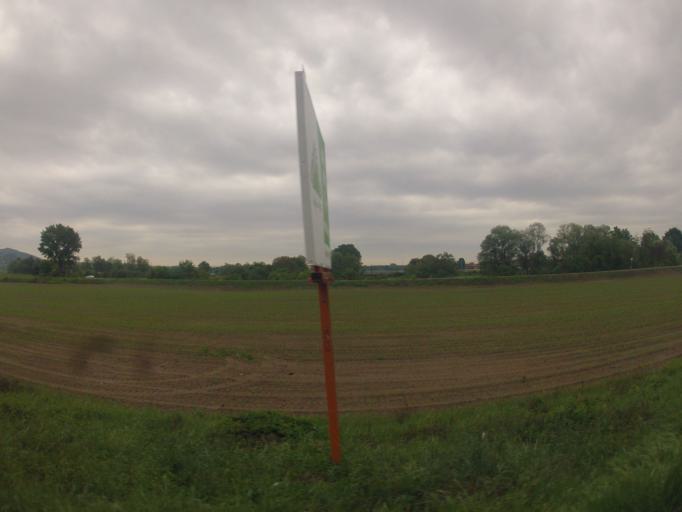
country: IT
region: Piedmont
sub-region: Provincia di Torino
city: Tagliaferro
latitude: 44.9777
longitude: 7.6704
